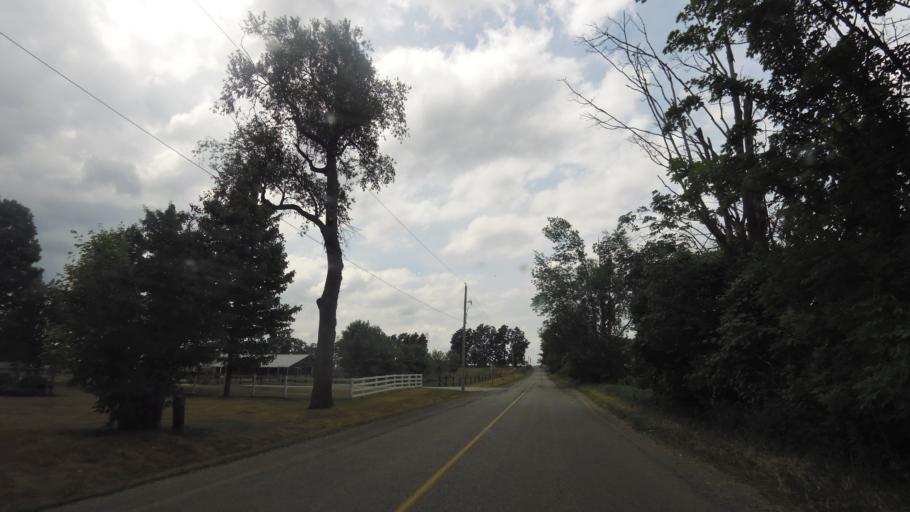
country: CA
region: Ontario
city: Brampton
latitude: 43.8405
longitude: -79.8735
